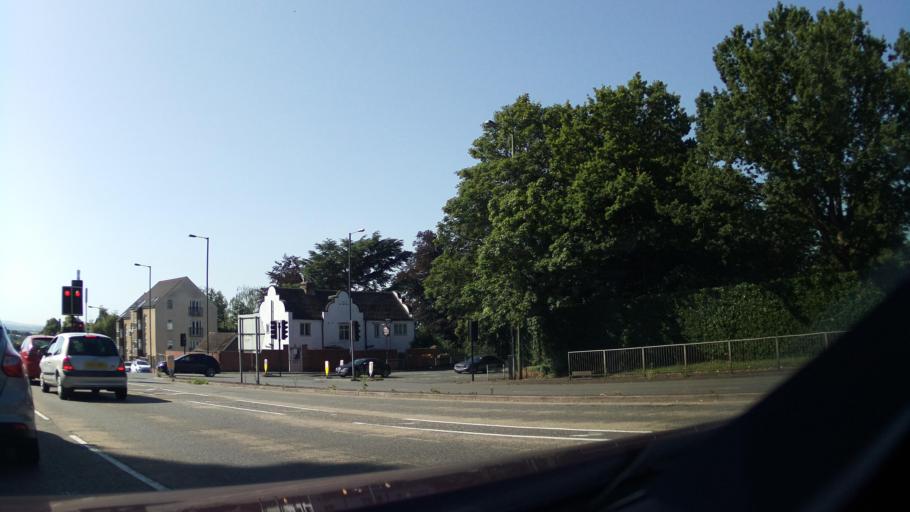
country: GB
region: England
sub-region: Derby
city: Derby
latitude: 52.9083
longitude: -1.5016
